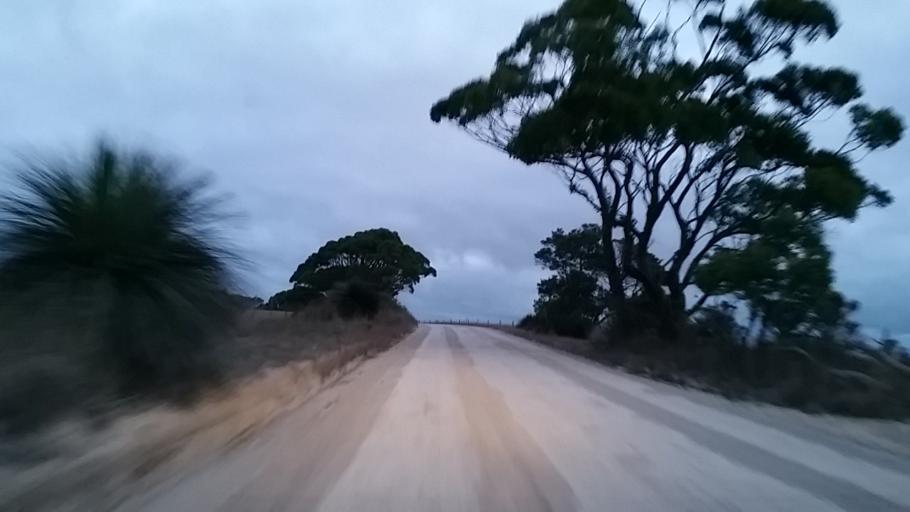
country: AU
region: South Australia
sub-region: Yankalilla
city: Normanville
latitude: -35.6097
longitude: 138.1997
